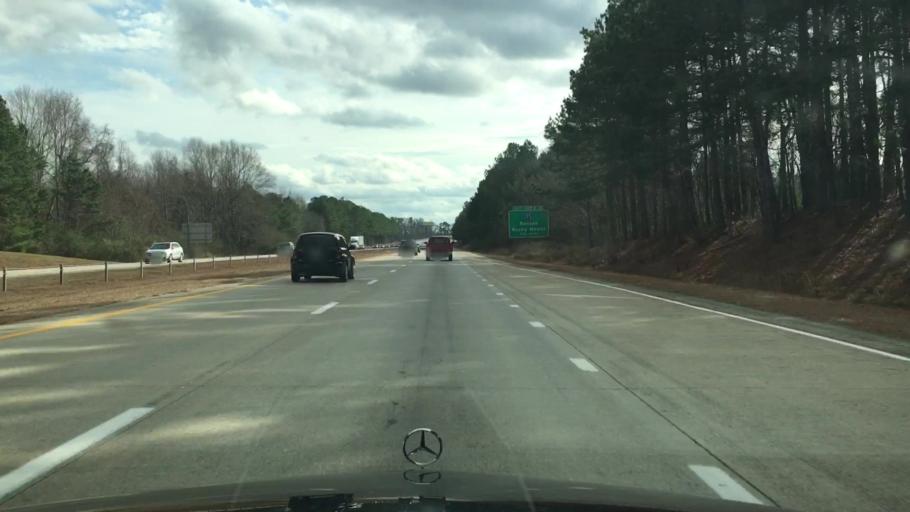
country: US
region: North Carolina
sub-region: Johnston County
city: Benson
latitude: 35.4182
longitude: -78.5280
